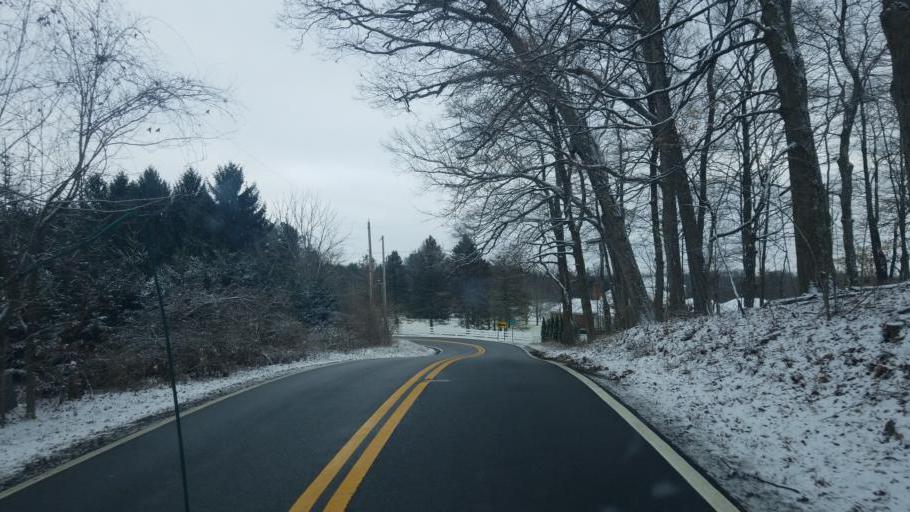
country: US
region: Ohio
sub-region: Franklin County
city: New Albany
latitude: 40.0485
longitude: -82.8380
